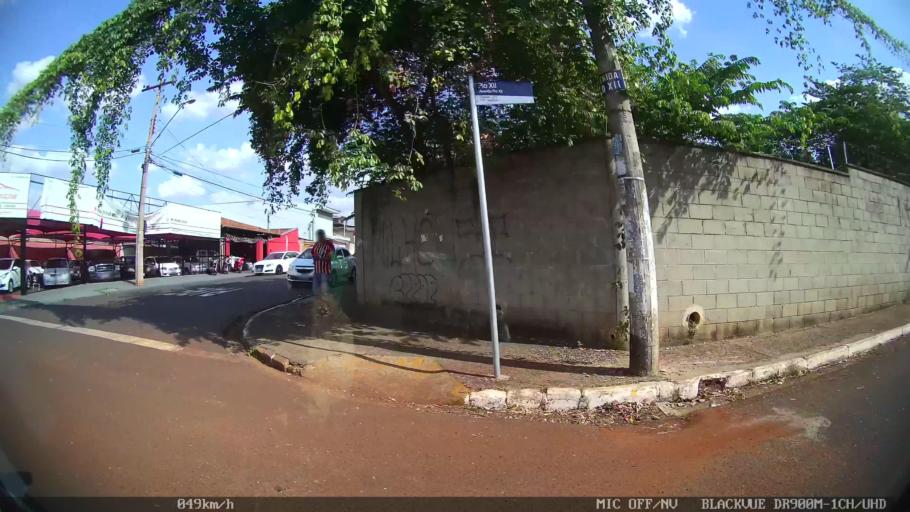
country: BR
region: Sao Paulo
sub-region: Ribeirao Preto
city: Ribeirao Preto
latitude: -21.1878
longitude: -47.8313
